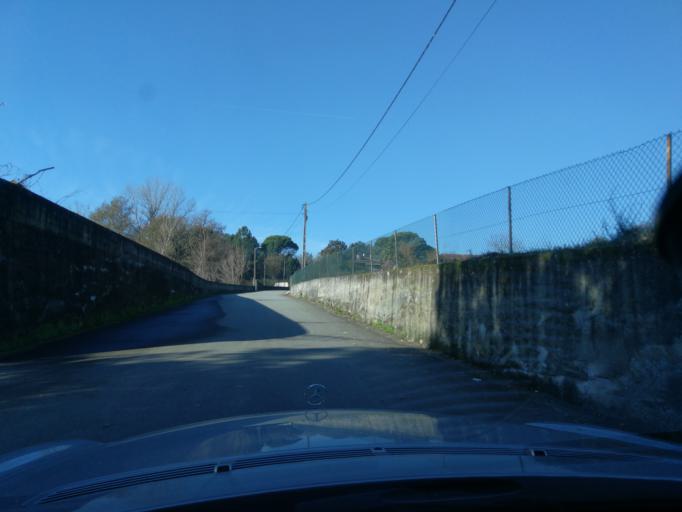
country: PT
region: Braga
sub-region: Braga
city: Adaufe
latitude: 41.6127
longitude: -8.3943
